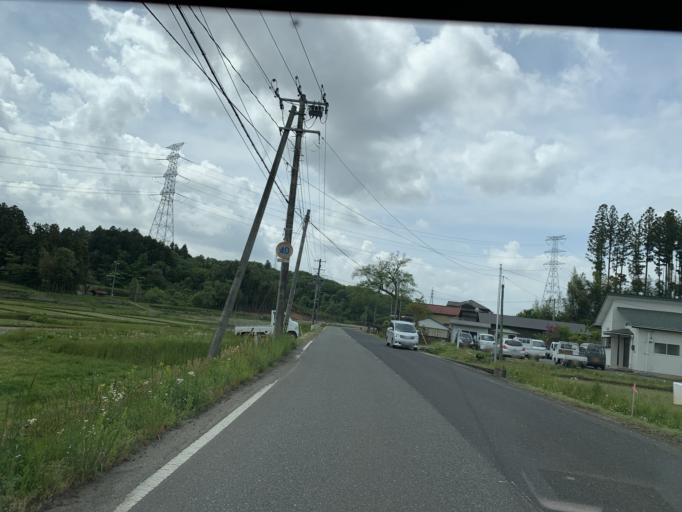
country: JP
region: Iwate
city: Ichinoseki
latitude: 38.8134
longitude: 141.0210
